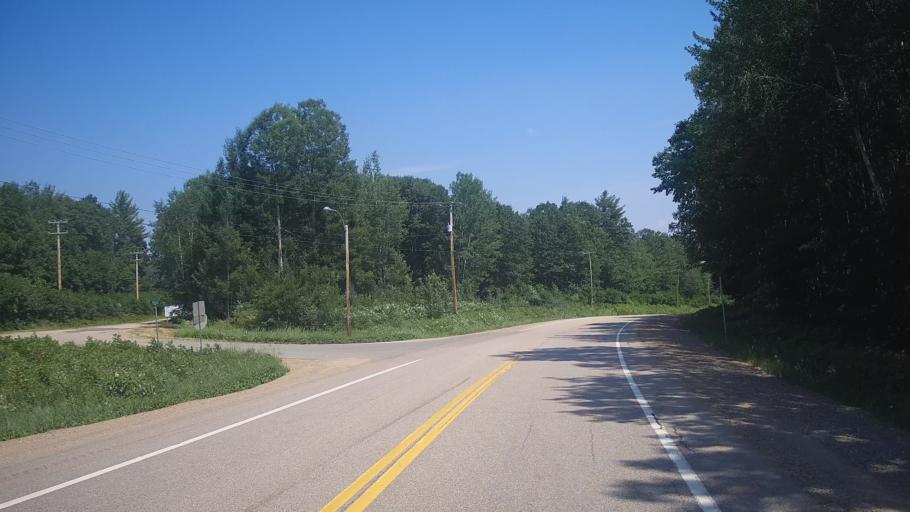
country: CA
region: Quebec
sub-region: Outaouais
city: Fort-Coulonge
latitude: 45.9171
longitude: -76.9288
